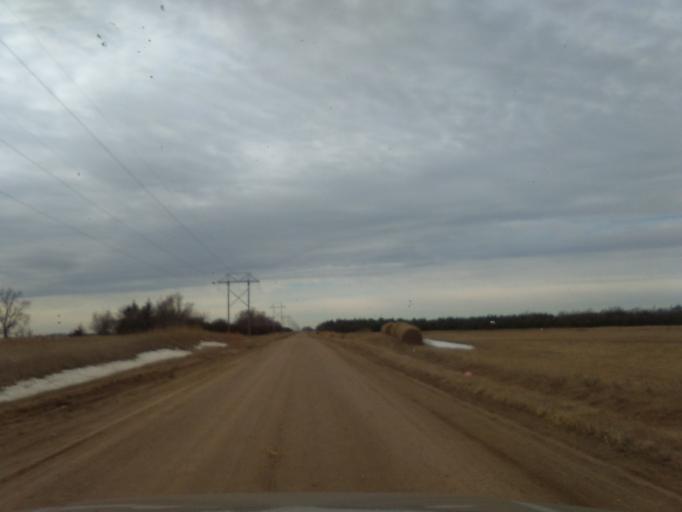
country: US
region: Nebraska
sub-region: Buffalo County
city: Gibbon
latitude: 40.6549
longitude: -98.7702
